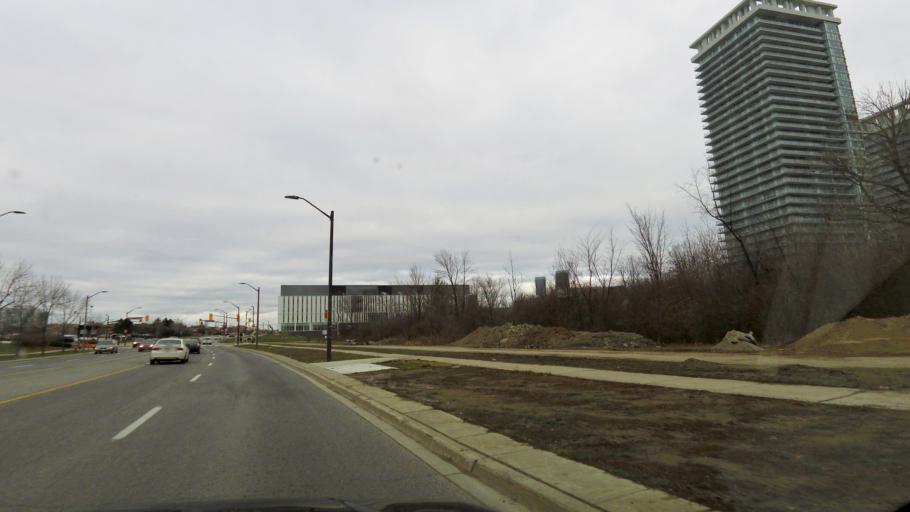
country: CA
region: Ontario
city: Mississauga
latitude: 43.5903
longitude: -79.6512
